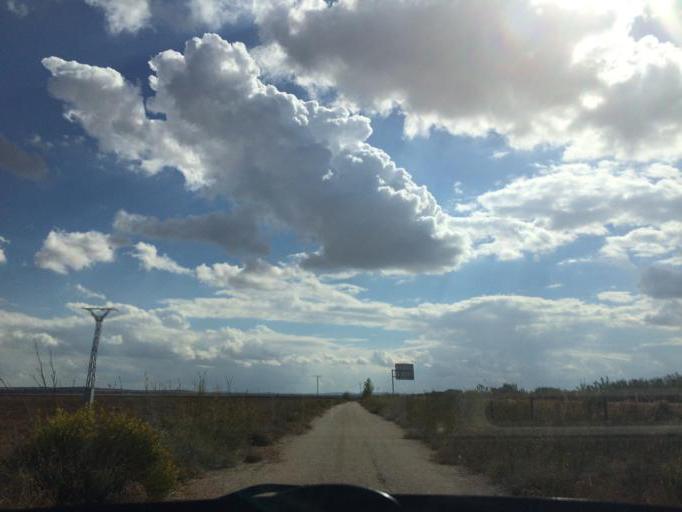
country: ES
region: Castille-La Mancha
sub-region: Provincia de Albacete
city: Albacete
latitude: 38.9595
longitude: -1.8206
